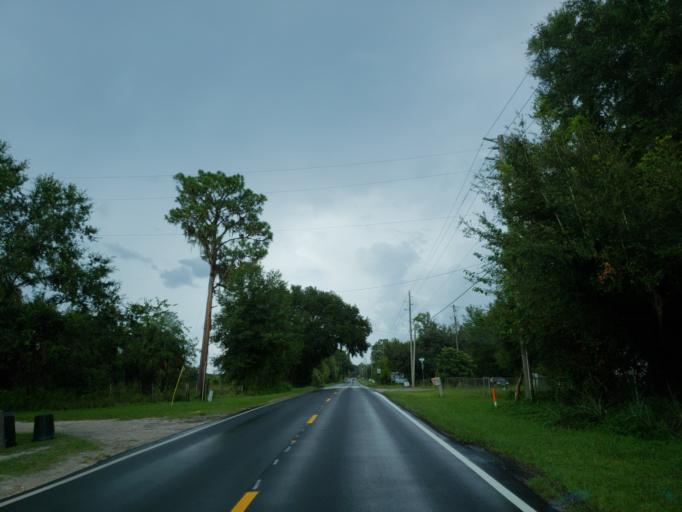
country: US
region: Florida
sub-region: Pasco County
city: Land O' Lakes
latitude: 28.2880
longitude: -82.4344
